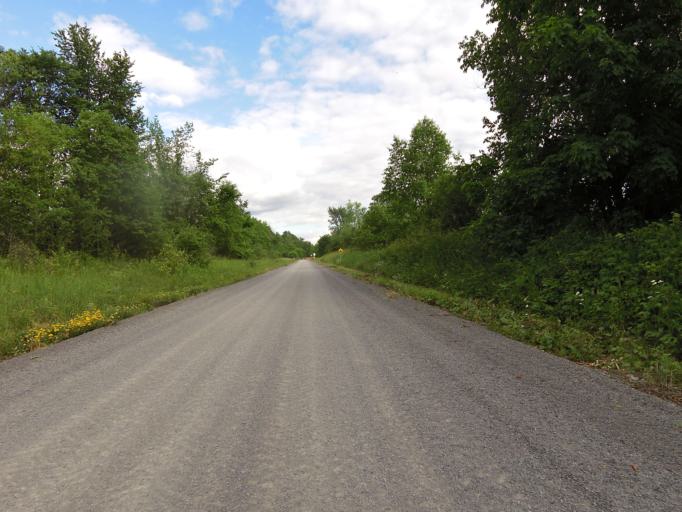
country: CA
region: Ontario
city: Arnprior
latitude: 45.3044
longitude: -76.2703
